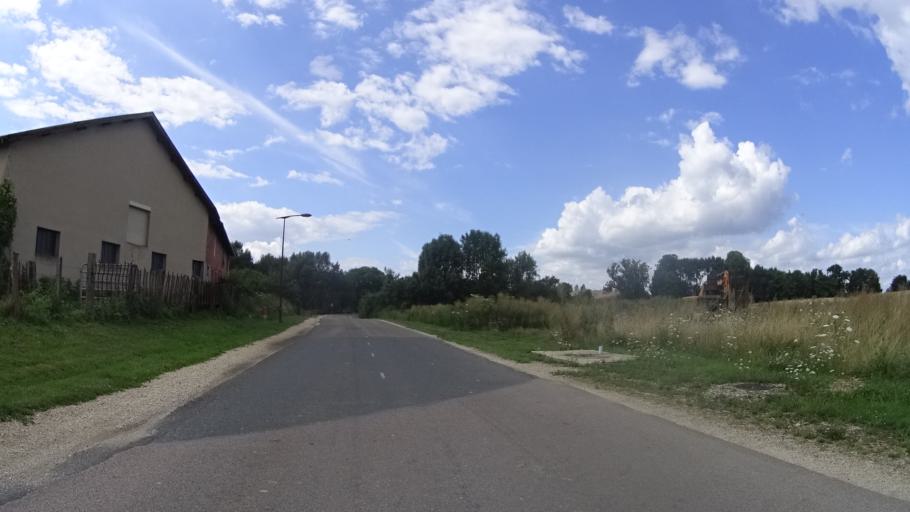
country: FR
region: Champagne-Ardenne
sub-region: Departement de la Marne
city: Pargny-sur-Saulx
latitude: 48.6917
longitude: 4.8047
